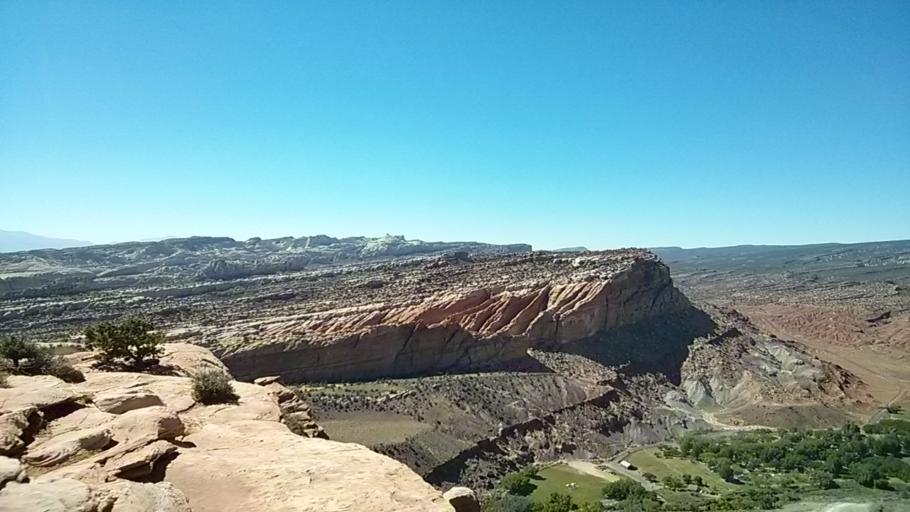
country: US
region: Utah
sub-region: Wayne County
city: Loa
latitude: 38.2911
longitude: -111.2493
